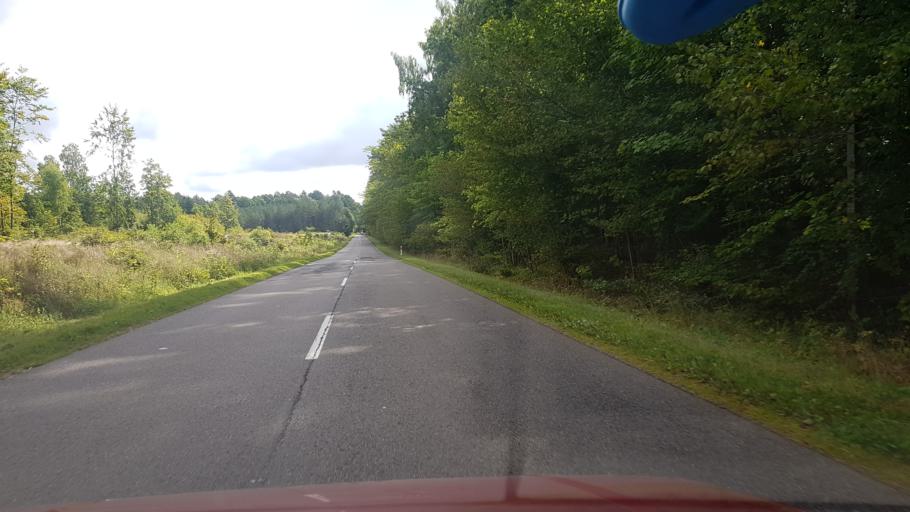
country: PL
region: West Pomeranian Voivodeship
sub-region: Powiat koszalinski
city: Polanow
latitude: 54.1151
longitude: 16.7680
